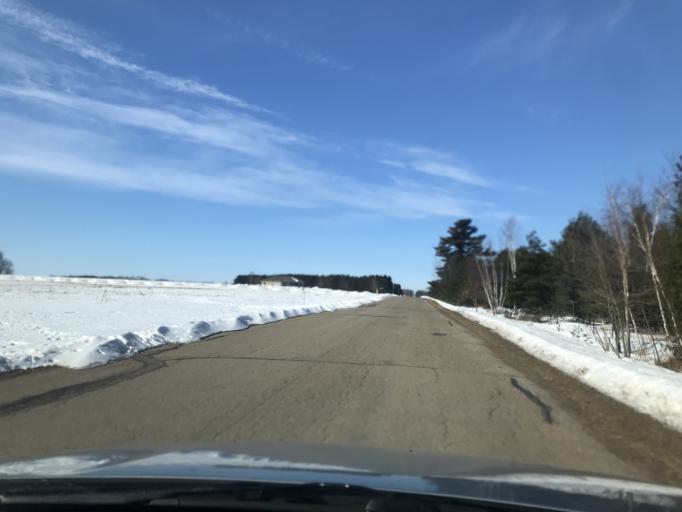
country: US
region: Wisconsin
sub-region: Oconto County
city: Oconto Falls
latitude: 44.9387
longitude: -88.2068
